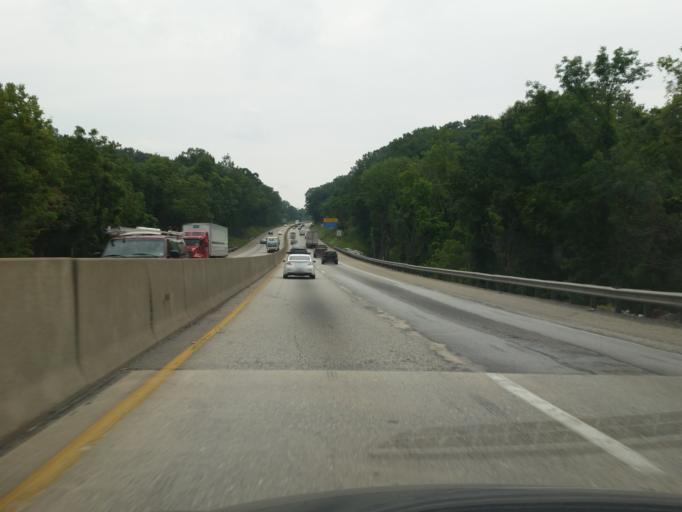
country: US
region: Pennsylvania
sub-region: York County
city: Valley Green
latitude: 40.1035
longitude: -76.7792
